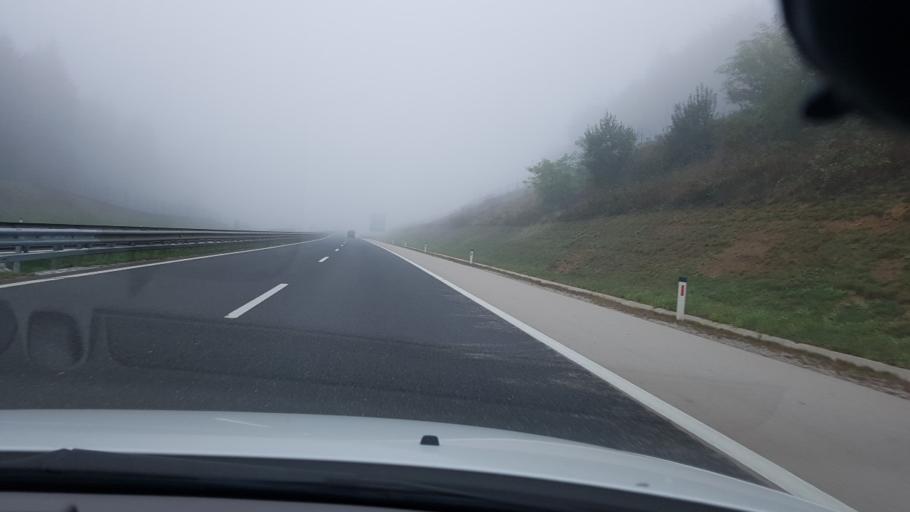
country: SI
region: Mirna Pec
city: Mirna Pec
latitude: 45.8870
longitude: 15.0688
